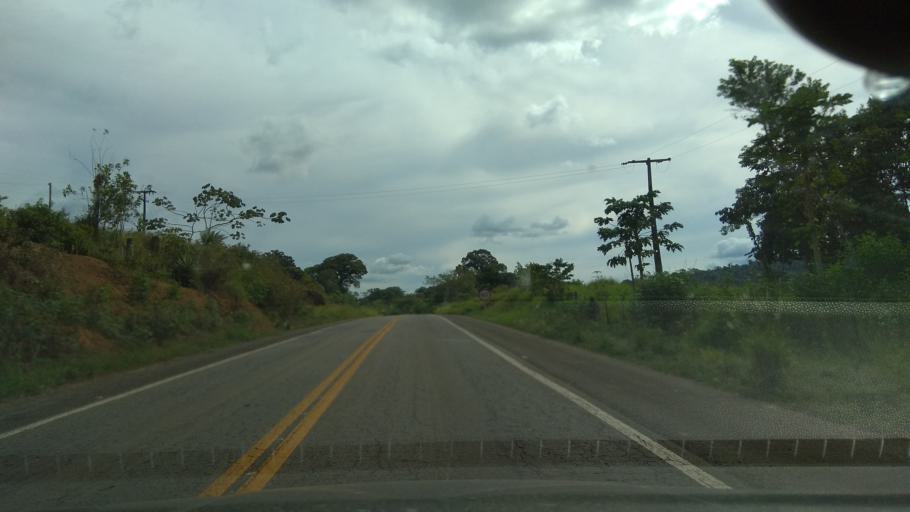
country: BR
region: Bahia
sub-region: Ubata
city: Ubata
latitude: -14.2291
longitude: -39.4434
